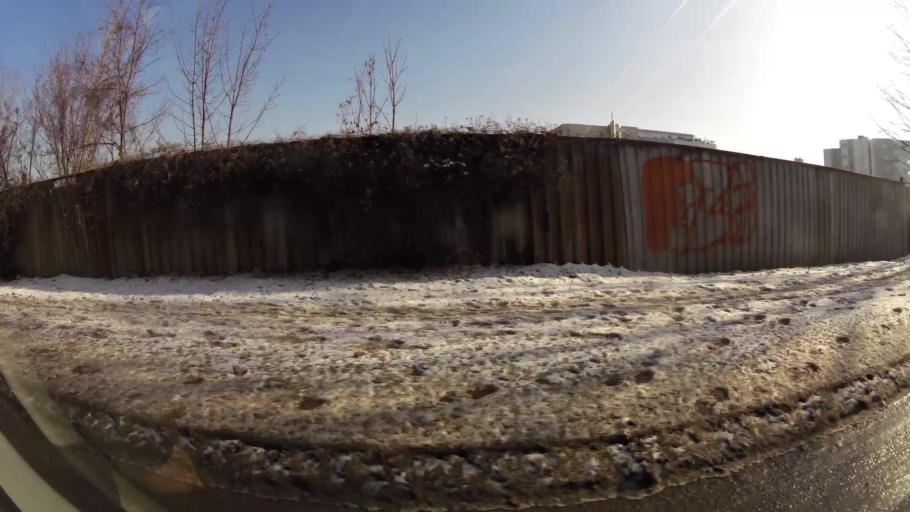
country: BG
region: Sofia-Capital
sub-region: Stolichna Obshtina
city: Sofia
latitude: 42.6618
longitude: 23.3211
